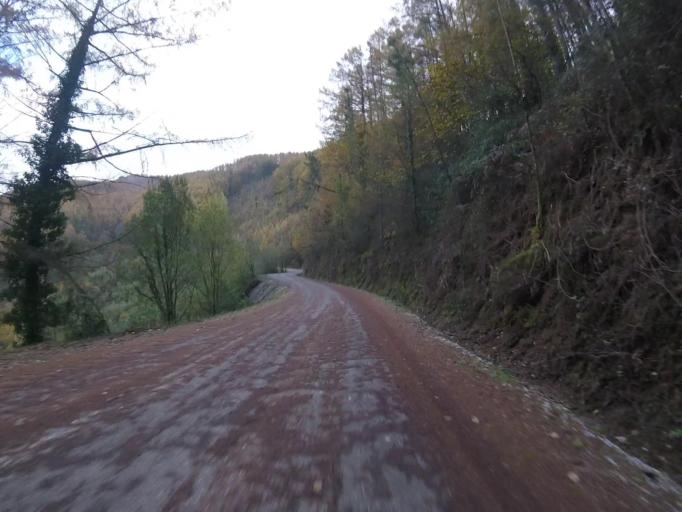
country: ES
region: Navarre
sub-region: Provincia de Navarra
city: Arano
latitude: 43.2140
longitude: -1.8560
